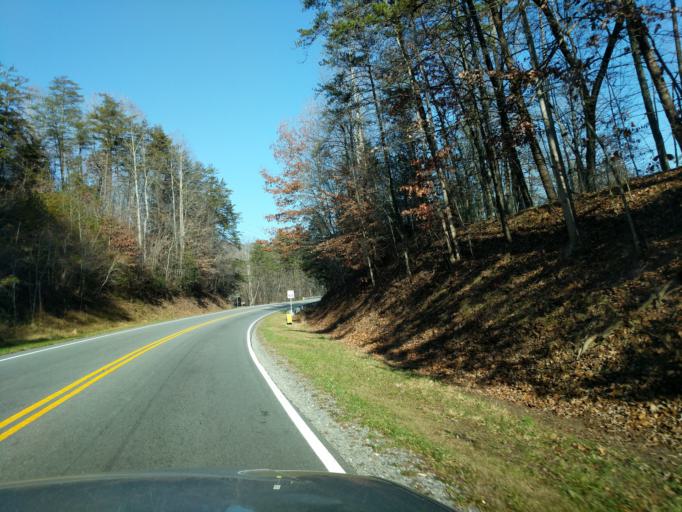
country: US
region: North Carolina
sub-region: McDowell County
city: West Marion
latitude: 35.5531
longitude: -81.9678
